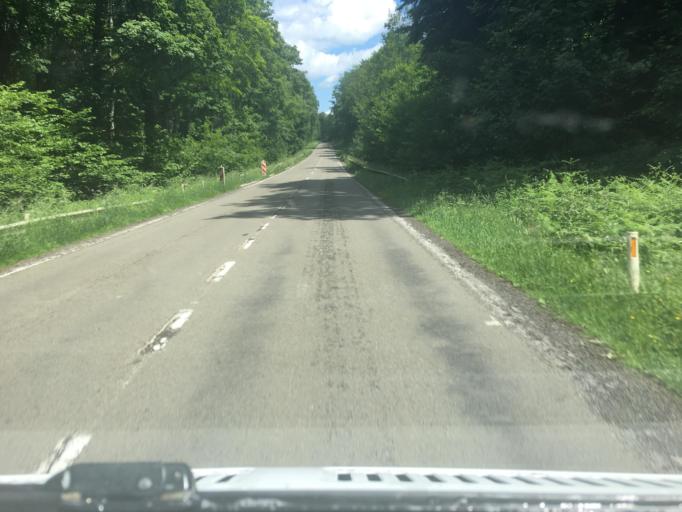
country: BE
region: Wallonia
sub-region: Province du Luxembourg
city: Florenville
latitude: 49.6694
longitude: 5.3338
